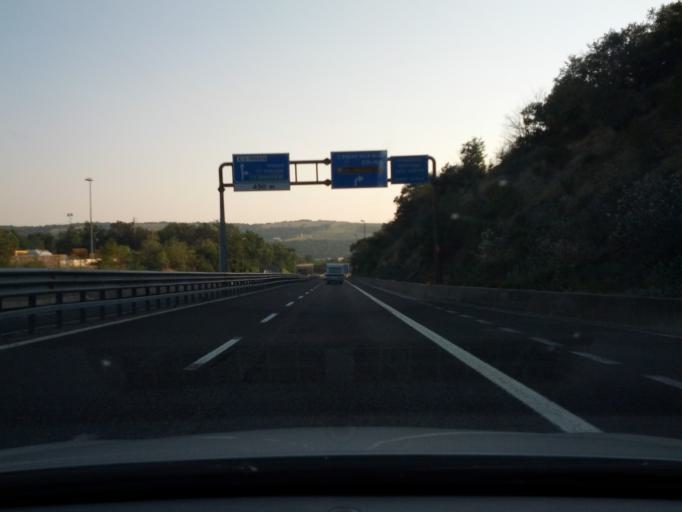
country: IT
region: Friuli Venezia Giulia
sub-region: Provincia di Trieste
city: Domio
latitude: 45.6118
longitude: 13.8437
